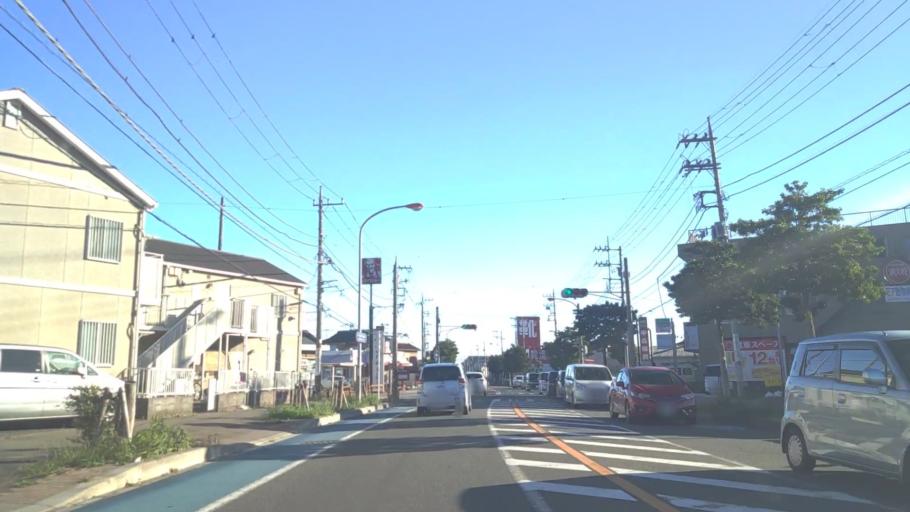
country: JP
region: Kanagawa
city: Chigasaki
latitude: 35.3499
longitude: 139.3969
